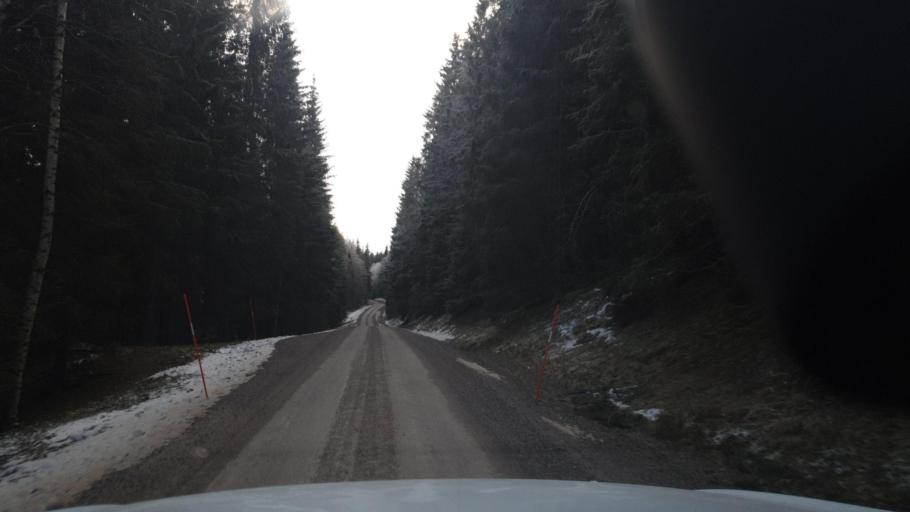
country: SE
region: Vaermland
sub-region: Eda Kommun
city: Charlottenberg
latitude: 60.0661
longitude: 12.5389
